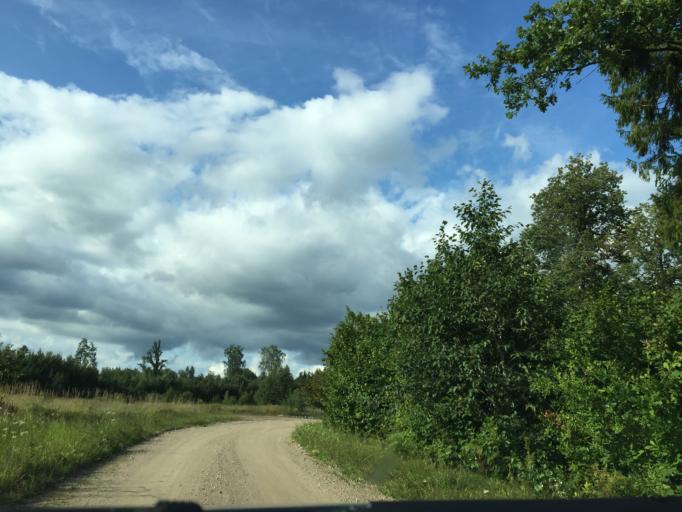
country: LV
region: Kegums
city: Kegums
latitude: 56.8219
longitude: 24.7566
